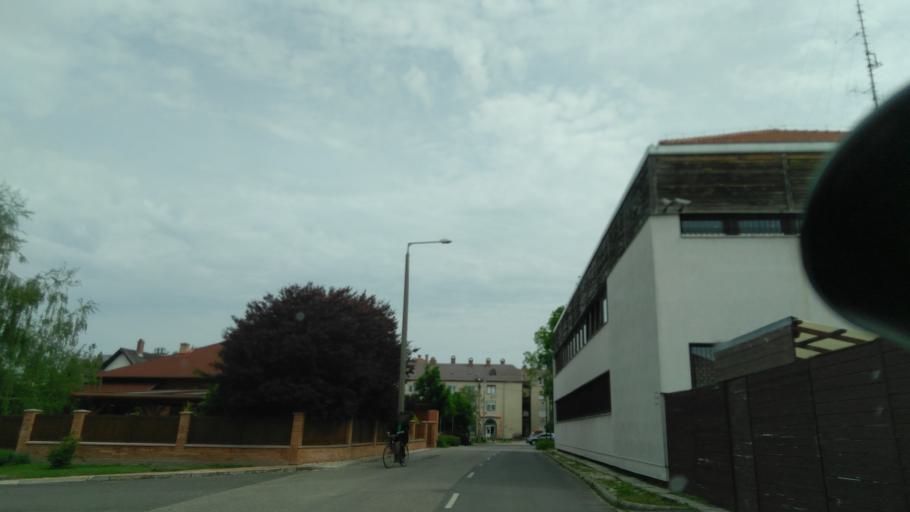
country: HU
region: Bekes
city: Szeghalom
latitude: 47.0144
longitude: 21.1734
